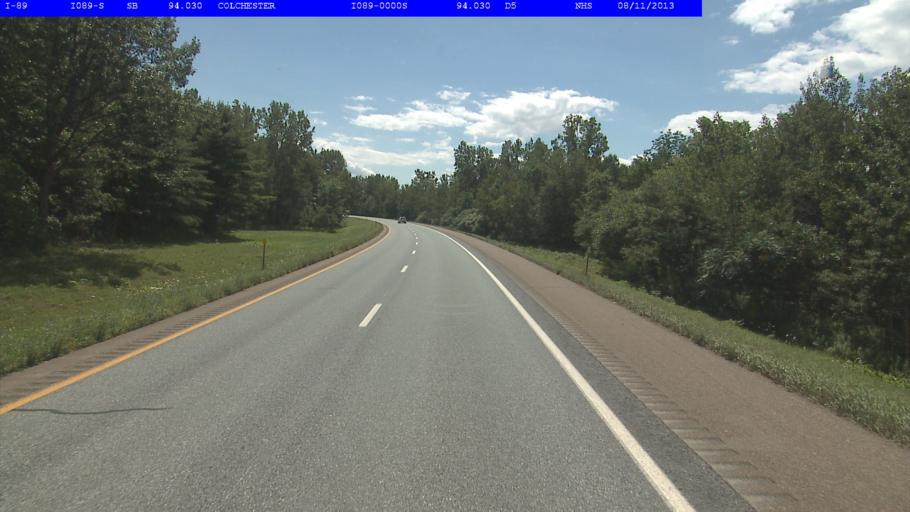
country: US
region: Vermont
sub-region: Chittenden County
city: Winooski
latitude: 44.5389
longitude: -73.1993
